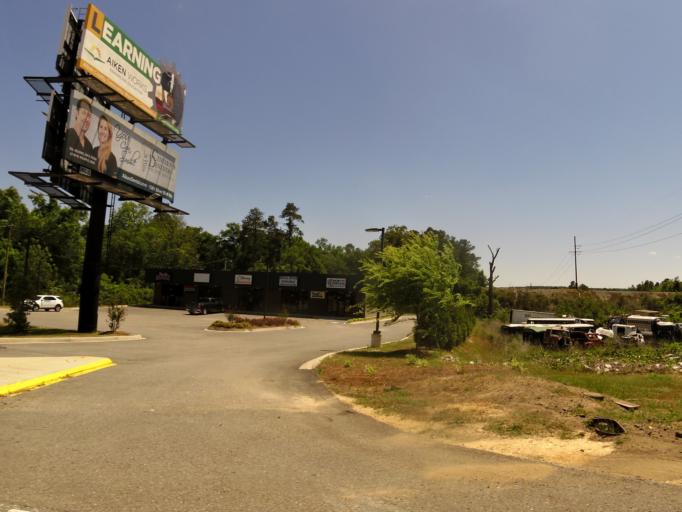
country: US
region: South Carolina
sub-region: Aiken County
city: Warrenville
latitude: 33.5612
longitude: -81.7802
